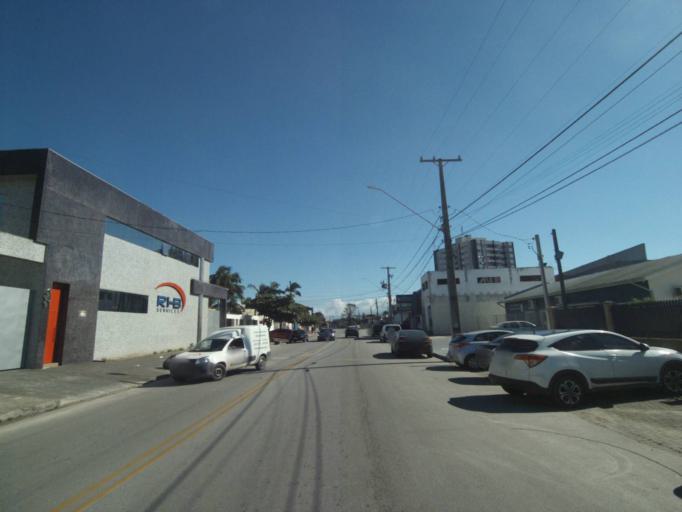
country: BR
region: Parana
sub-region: Paranagua
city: Paranagua
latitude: -25.5202
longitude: -48.5188
